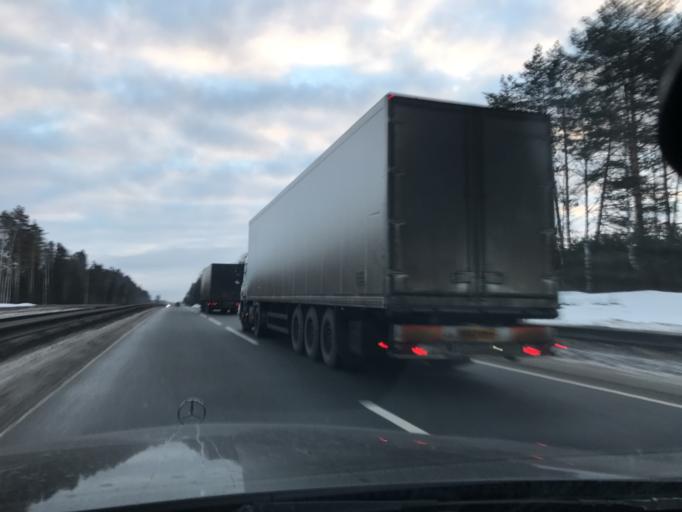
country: RU
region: Vladimir
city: Stepantsevo
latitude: 56.2320
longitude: 41.7727
